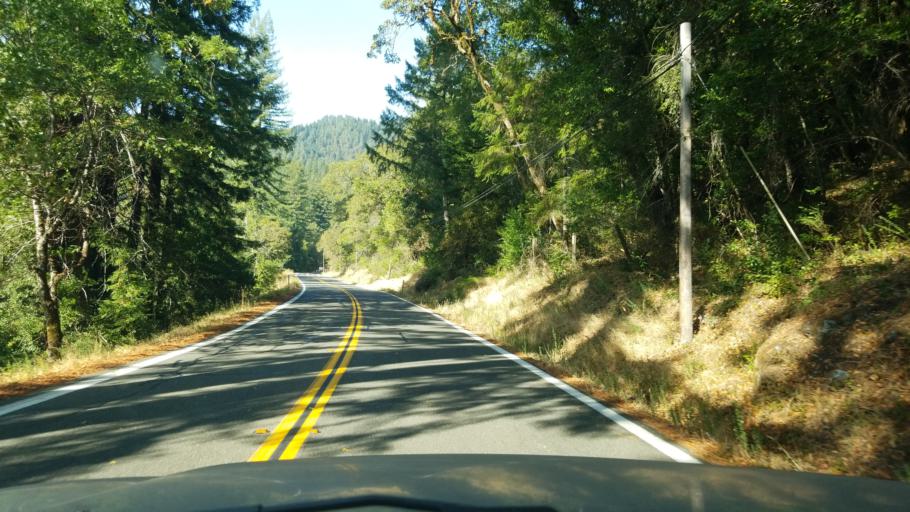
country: US
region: California
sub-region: Humboldt County
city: Redway
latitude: 40.1886
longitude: -123.7697
